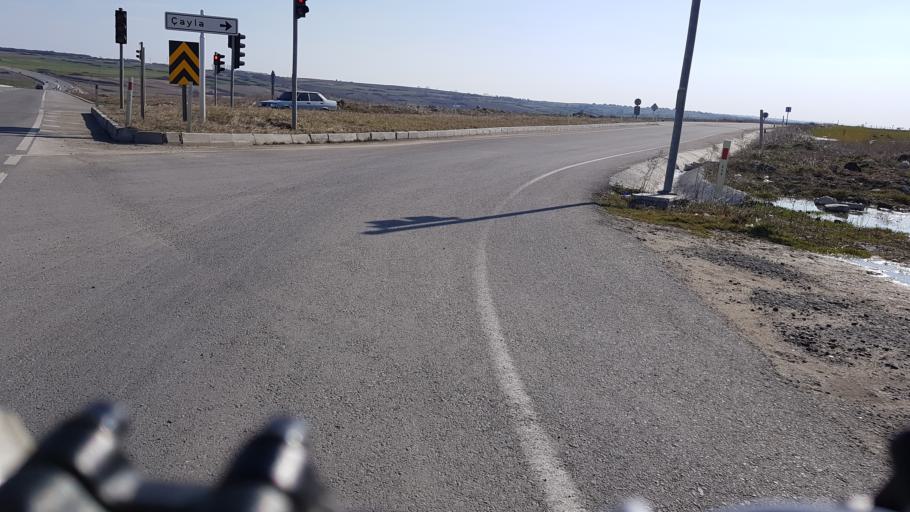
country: TR
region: Tekirdag
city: Saray
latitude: 41.4314
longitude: 27.9092
